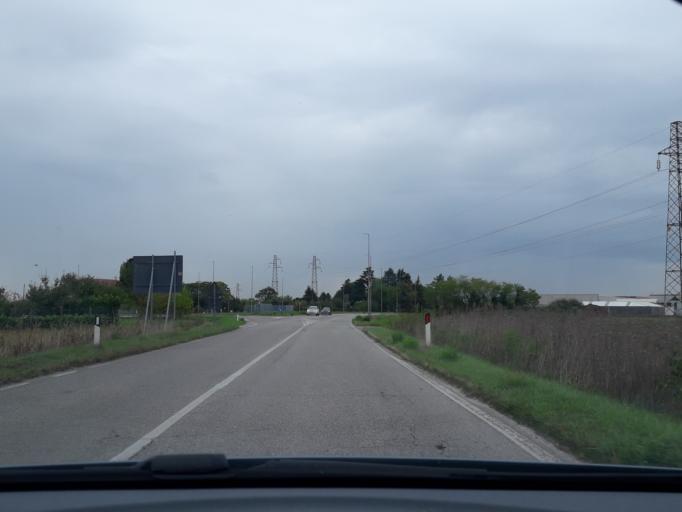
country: IT
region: Friuli Venezia Giulia
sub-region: Provincia di Udine
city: Feletto Umberto
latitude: 46.0957
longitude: 13.2547
